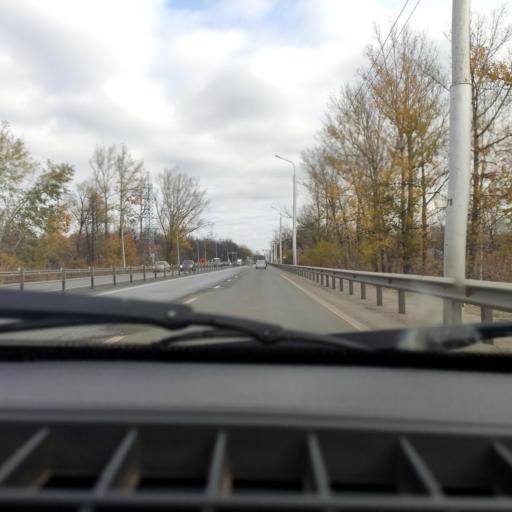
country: RU
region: Bashkortostan
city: Ufa
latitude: 54.6983
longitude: 55.8965
